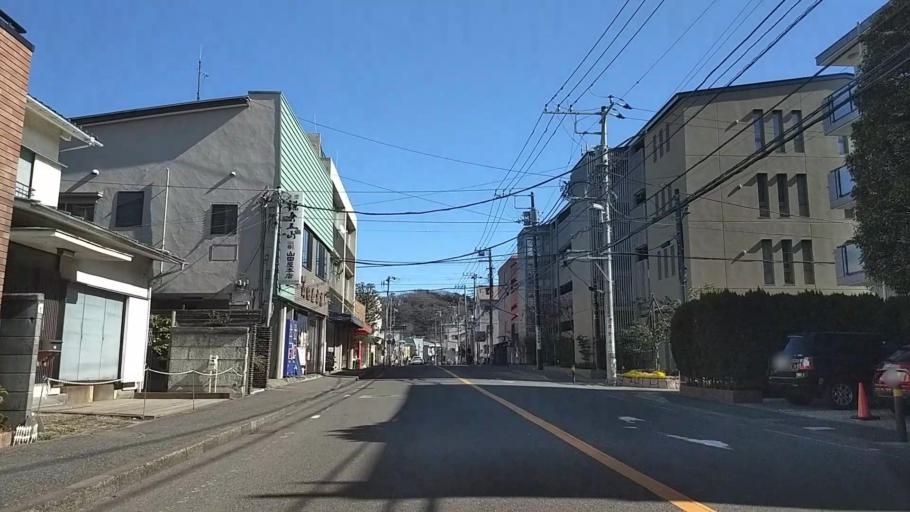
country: JP
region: Kanagawa
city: Kamakura
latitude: 35.3236
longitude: 139.5599
